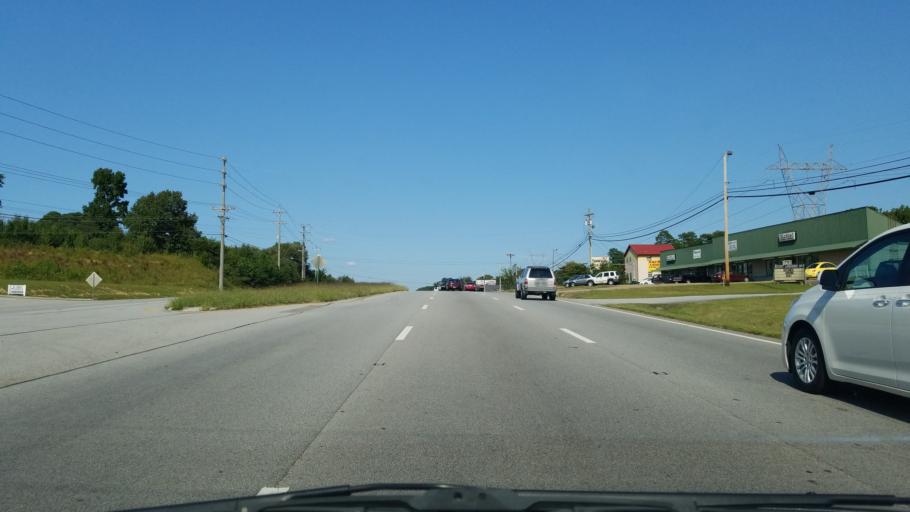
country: US
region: Tennessee
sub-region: Hamilton County
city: Harrison
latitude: 35.0955
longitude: -85.1757
